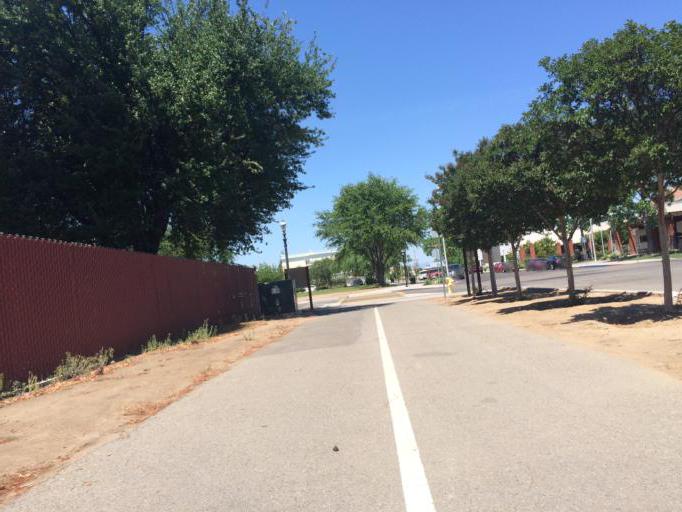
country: US
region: California
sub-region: Fresno County
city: Clovis
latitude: 36.8237
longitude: -119.6993
